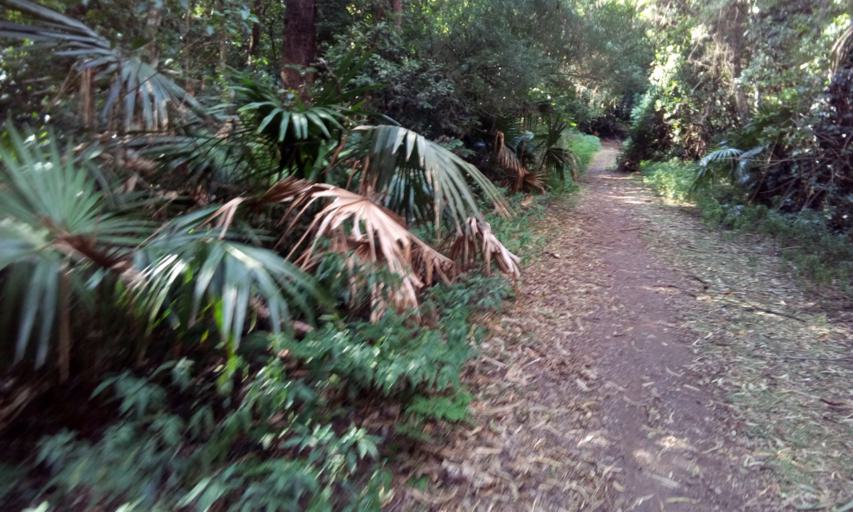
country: AU
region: New South Wales
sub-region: Wollongong
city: Cordeaux Heights
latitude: -34.4448
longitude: 150.8006
